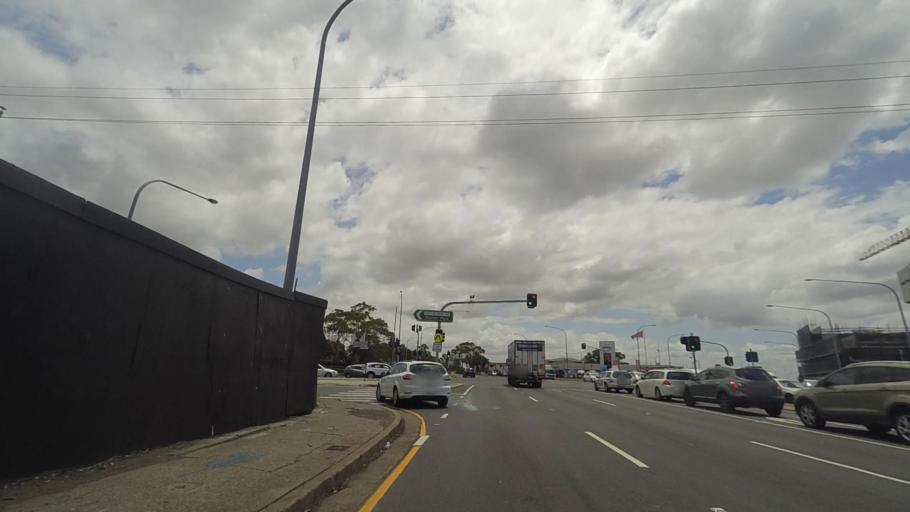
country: AU
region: New South Wales
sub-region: Fairfield
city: Liverpool
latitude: -33.9291
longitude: 150.9178
